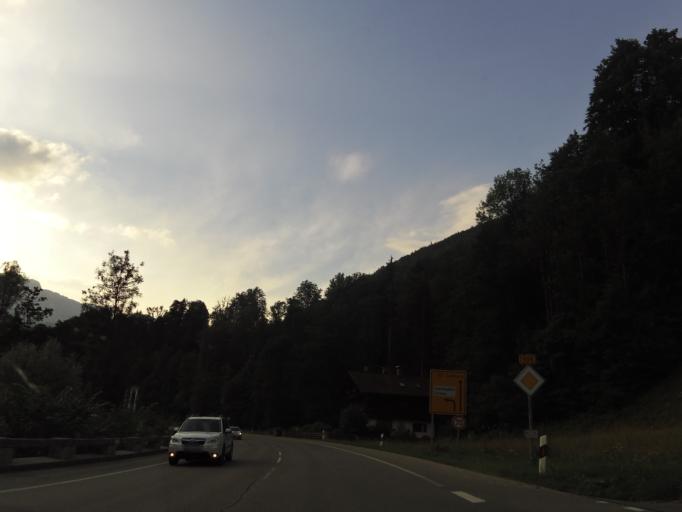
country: DE
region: Bavaria
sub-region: Upper Bavaria
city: Marktschellenberg
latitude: 47.6557
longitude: 13.0418
